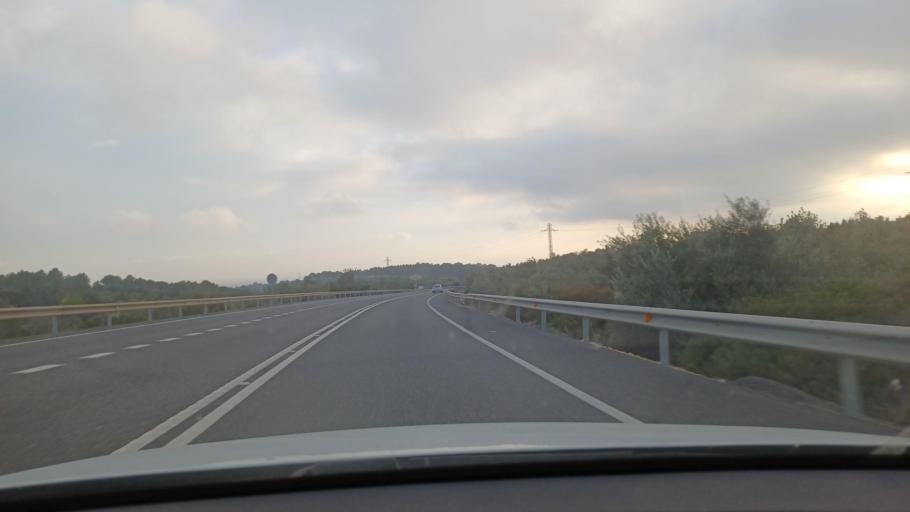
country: ES
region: Catalonia
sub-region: Provincia de Tarragona
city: El Perello
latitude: 40.8562
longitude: 0.7144
